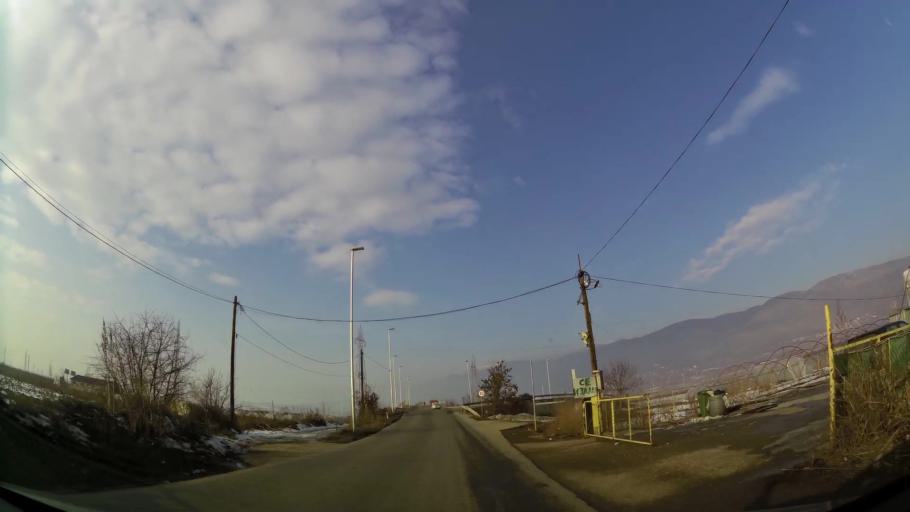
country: MK
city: Creshevo
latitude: 42.0300
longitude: 21.5123
